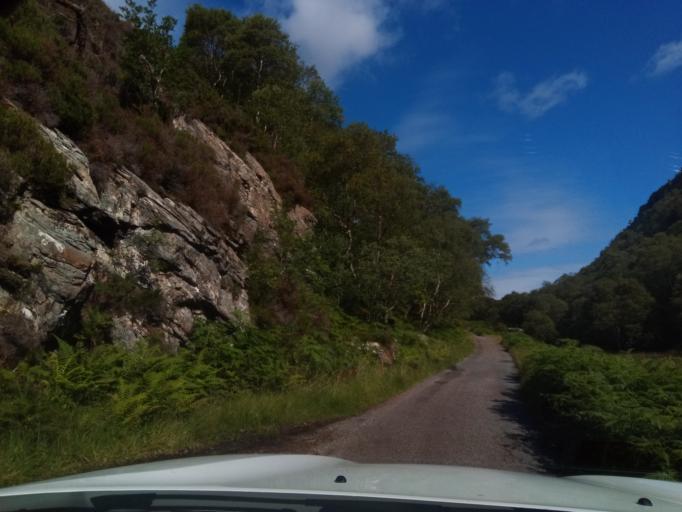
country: GB
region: Scotland
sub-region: Argyll and Bute
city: Isle Of Mull
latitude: 56.7688
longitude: -5.8232
